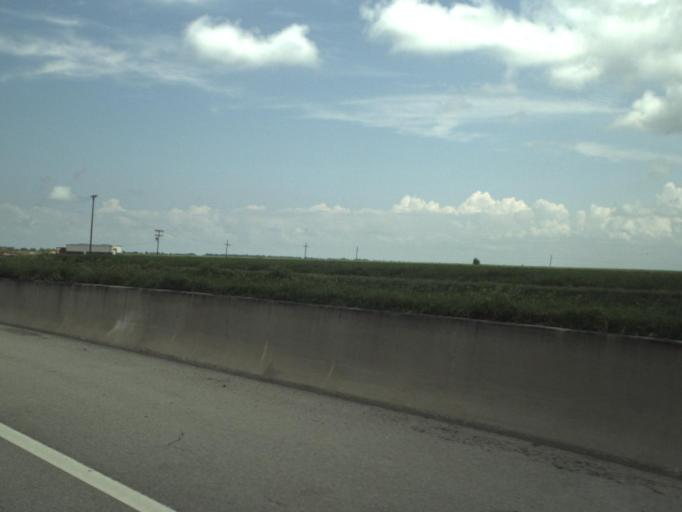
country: US
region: Florida
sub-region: Palm Beach County
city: Pahokee
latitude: 26.8365
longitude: -80.5947
